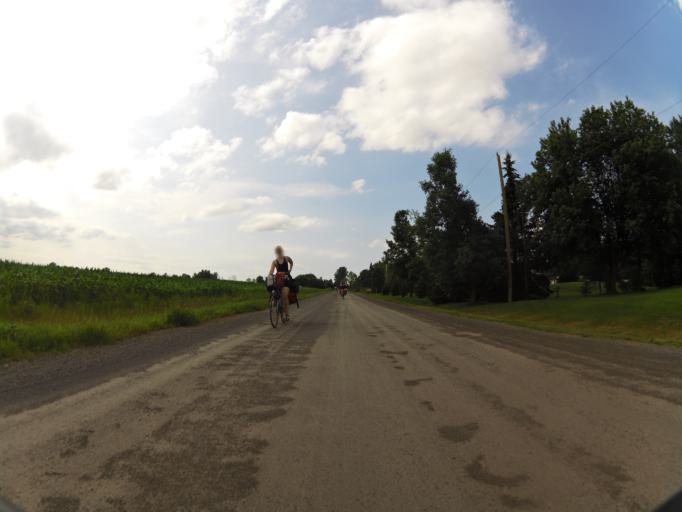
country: CA
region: Ontario
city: Bells Corners
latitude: 45.0762
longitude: -75.6060
